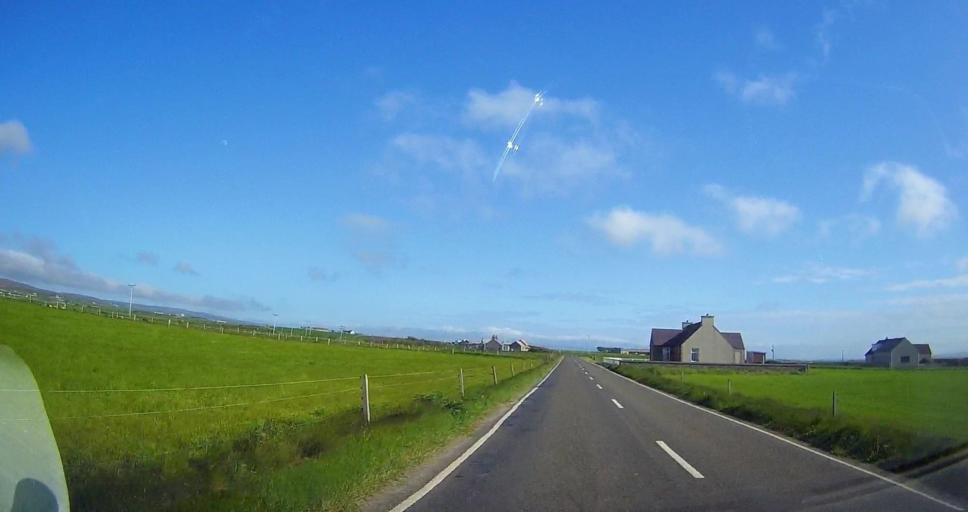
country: GB
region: Scotland
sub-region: Orkney Islands
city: Stromness
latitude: 59.0804
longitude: -3.2528
